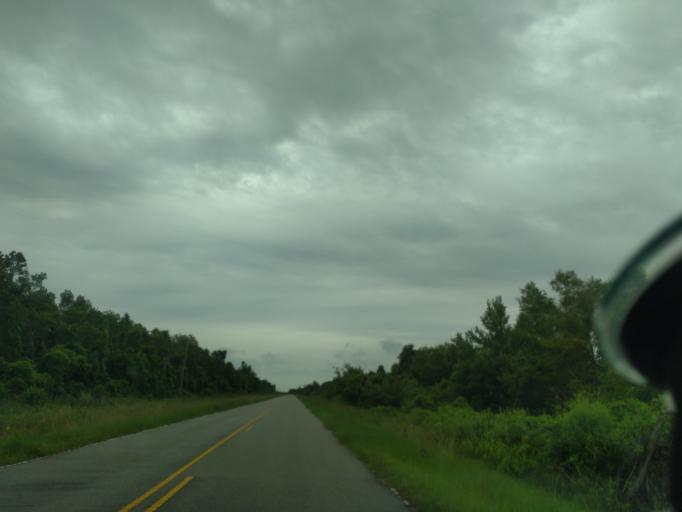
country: US
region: North Carolina
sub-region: Beaufort County
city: Belhaven
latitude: 35.7504
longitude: -76.5065
